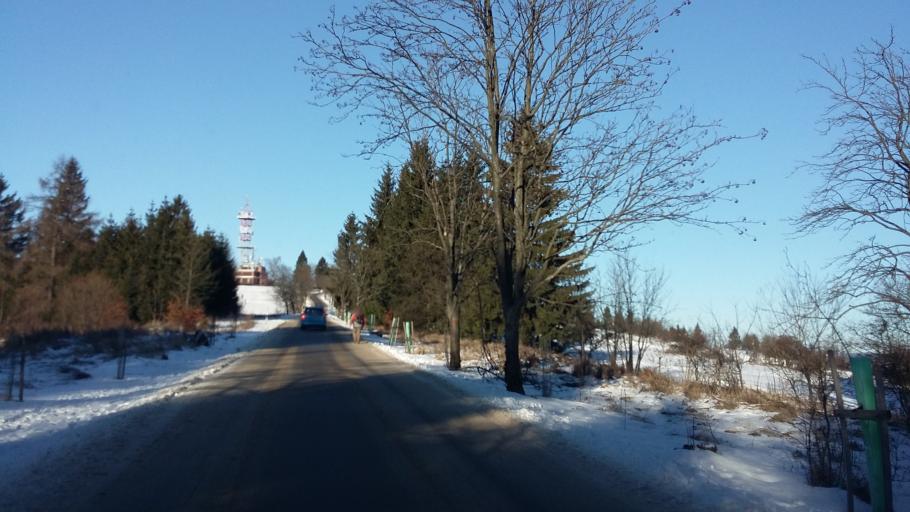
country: CZ
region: Liberecky
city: Zelezny Brod
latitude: 50.5920
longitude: 15.2687
